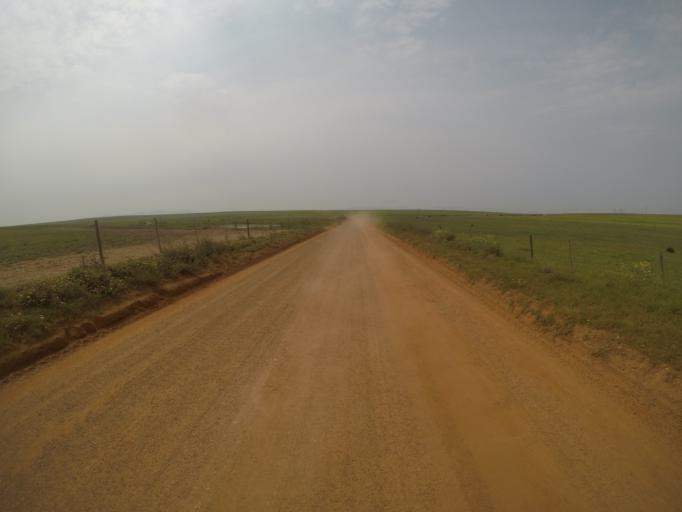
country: ZA
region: Western Cape
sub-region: City of Cape Town
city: Kraaifontein
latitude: -33.7240
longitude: 18.6670
